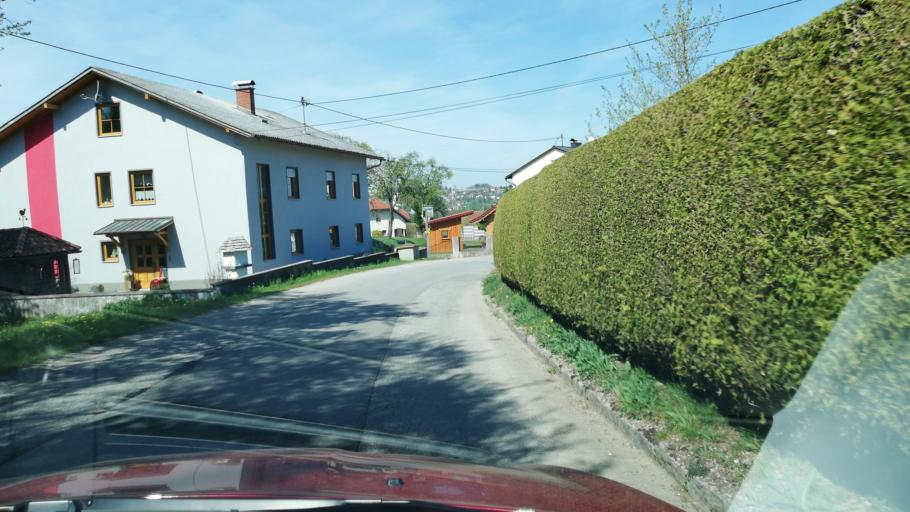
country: AT
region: Upper Austria
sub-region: Politischer Bezirk Kirchdorf an der Krems
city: Kremsmunster
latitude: 48.0499
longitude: 14.1522
